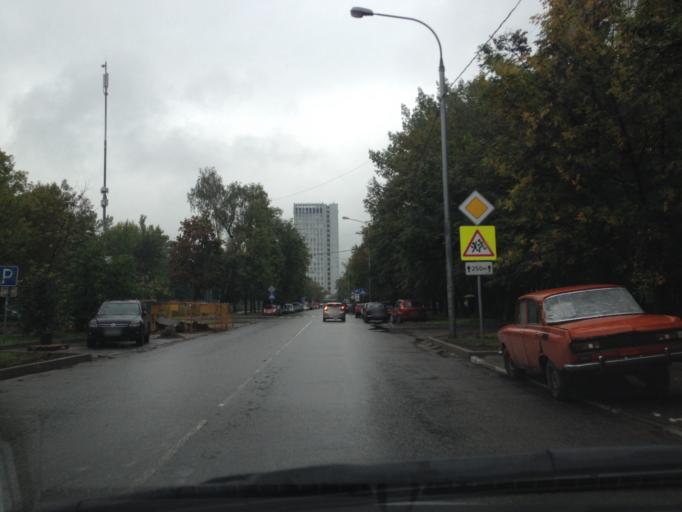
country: RU
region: Moscow
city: Metrogorodok
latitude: 55.8060
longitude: 37.8049
